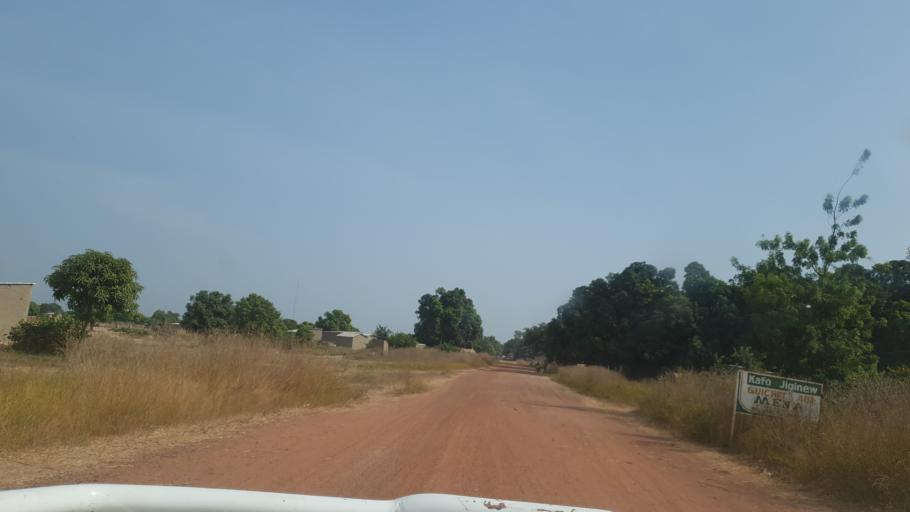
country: ML
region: Koulikoro
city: Dioila
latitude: 12.2210
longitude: -6.2109
